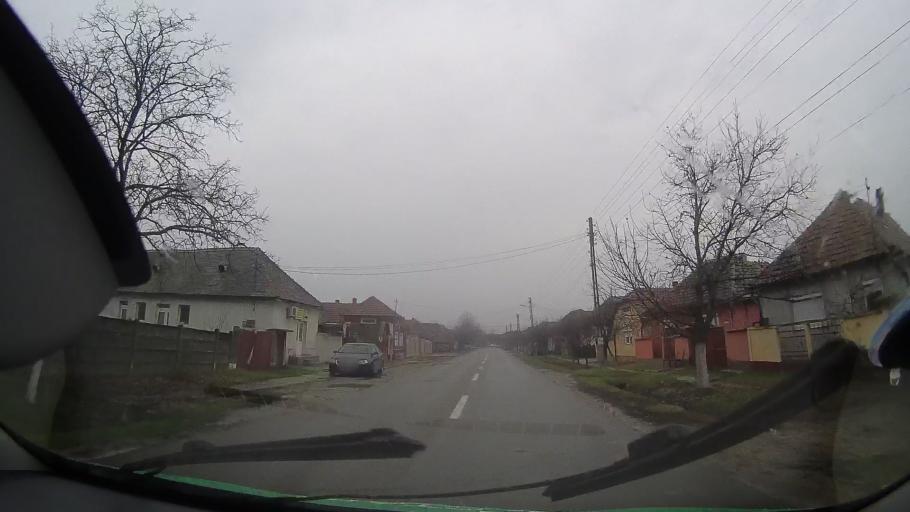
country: RO
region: Bihor
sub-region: Comuna Tulca
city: Tulca
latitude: 46.7899
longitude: 21.7730
